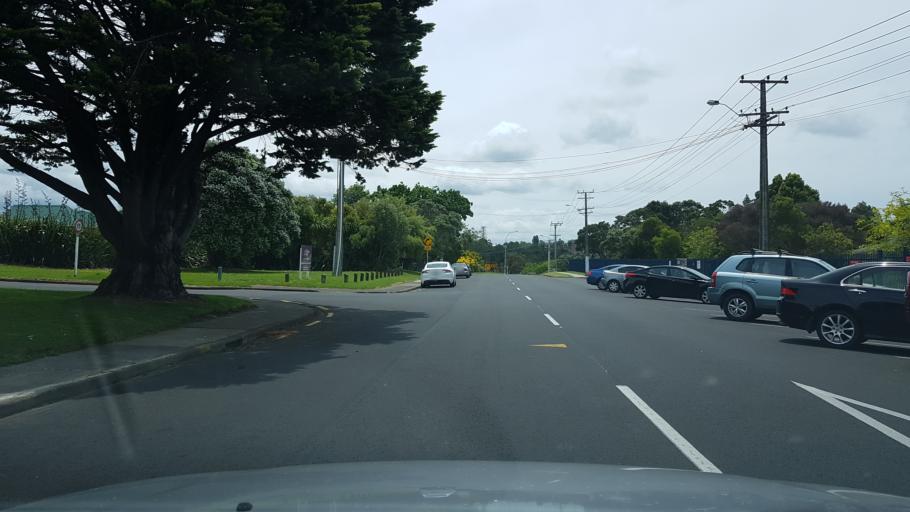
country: NZ
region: Auckland
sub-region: Auckland
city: North Shore
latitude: -36.8164
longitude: 174.7075
